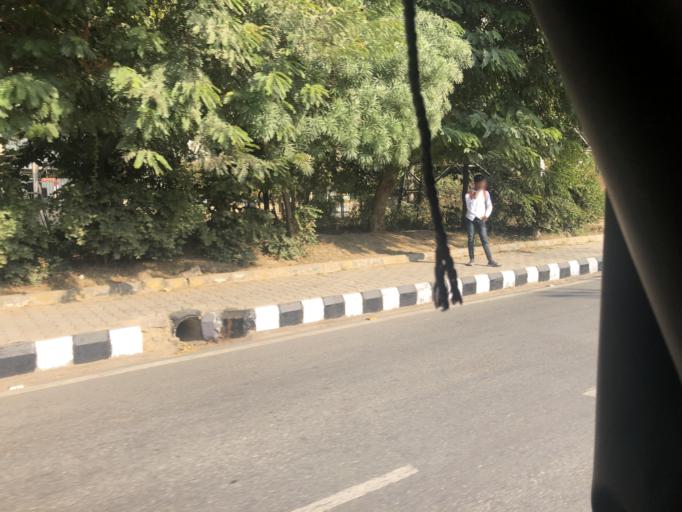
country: IN
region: Haryana
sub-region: Gurgaon
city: Gurgaon
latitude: 28.4491
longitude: 77.0781
